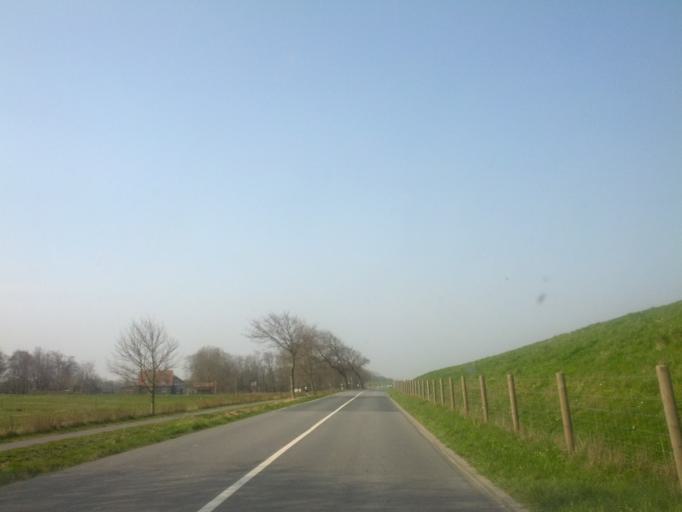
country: DE
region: Lower Saxony
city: Holtgast
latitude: 53.6718
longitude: 7.5557
